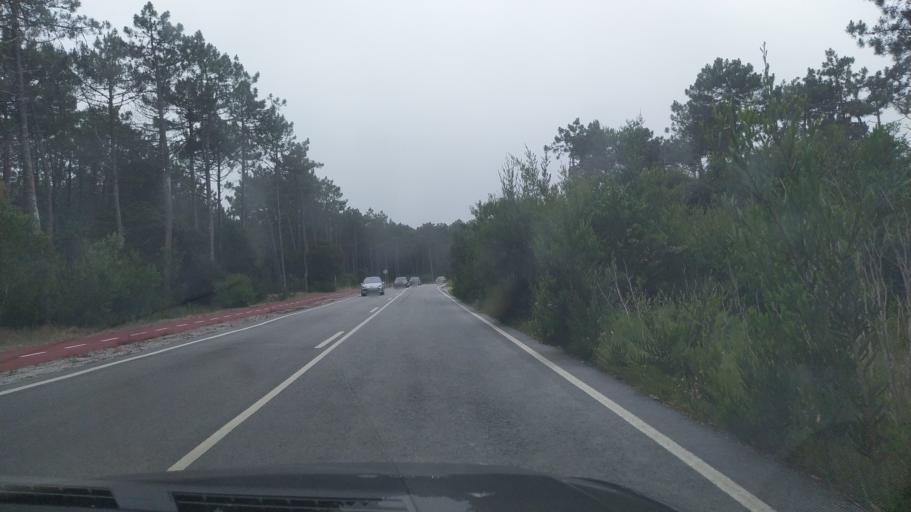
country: PT
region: Aveiro
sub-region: Ilhavo
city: Gafanha da Encarnacao
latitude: 40.5742
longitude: -8.7352
